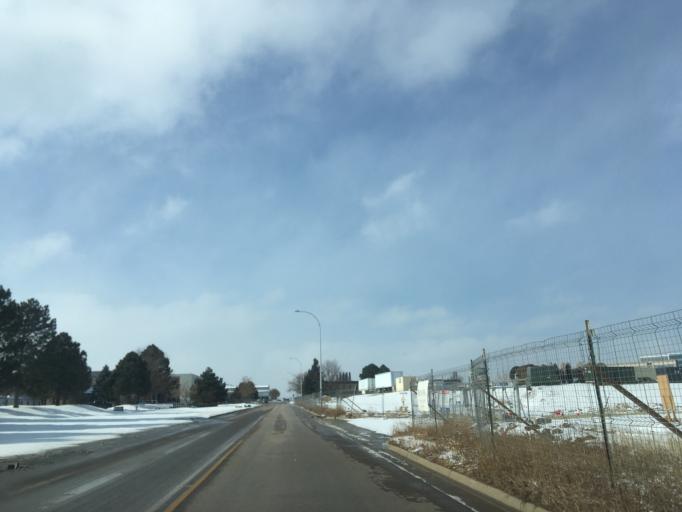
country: US
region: Colorado
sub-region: Broomfield County
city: Broomfield
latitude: 39.9109
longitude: -105.1046
